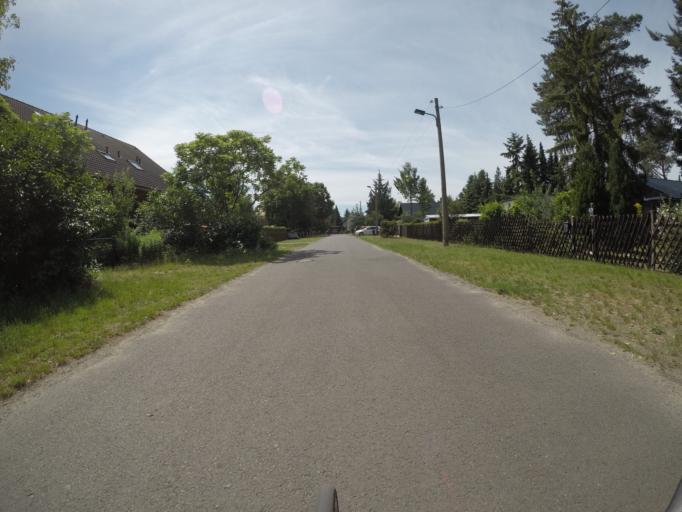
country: DE
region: Berlin
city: Friedrichshagen
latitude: 52.4752
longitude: 13.6108
